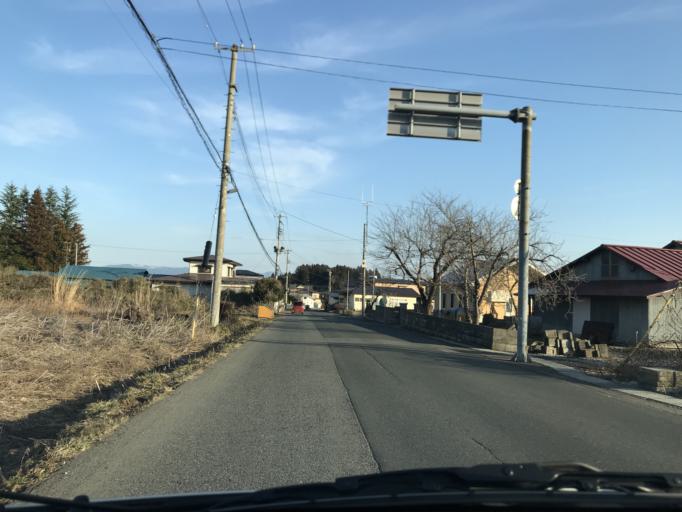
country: JP
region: Iwate
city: Kitakami
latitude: 39.2189
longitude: 141.1089
